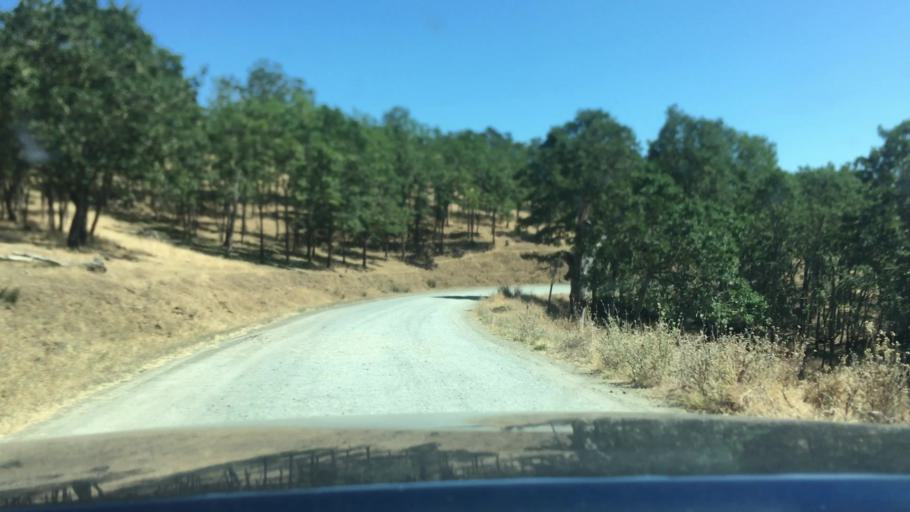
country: US
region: Oregon
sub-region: Douglas County
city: Winston
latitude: 43.1387
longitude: -123.4385
